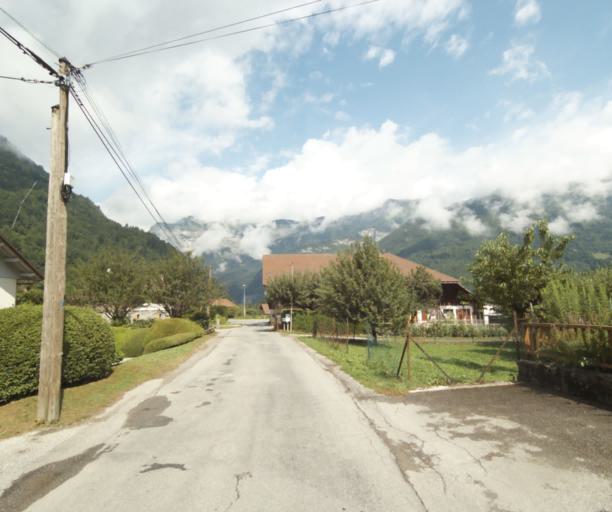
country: FR
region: Rhone-Alpes
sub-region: Departement de la Haute-Savoie
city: Thones
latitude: 45.8874
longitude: 6.3072
